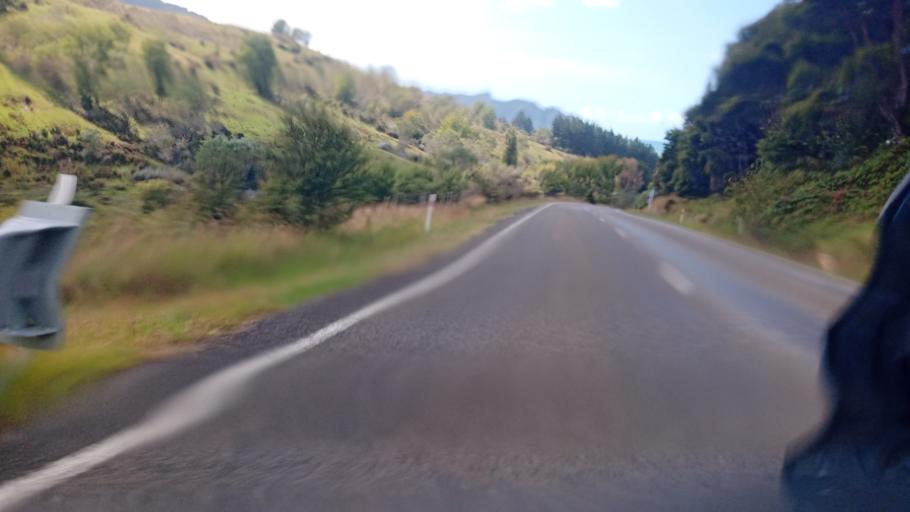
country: NZ
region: Gisborne
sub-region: Gisborne District
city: Gisborne
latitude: -38.1357
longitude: 178.3007
